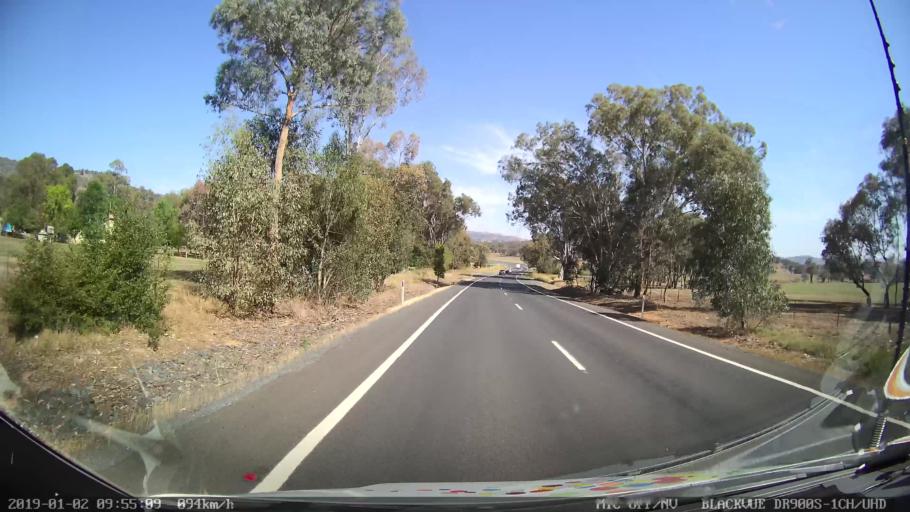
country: AU
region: New South Wales
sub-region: Tumut Shire
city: Tumut
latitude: -35.2266
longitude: 148.1916
